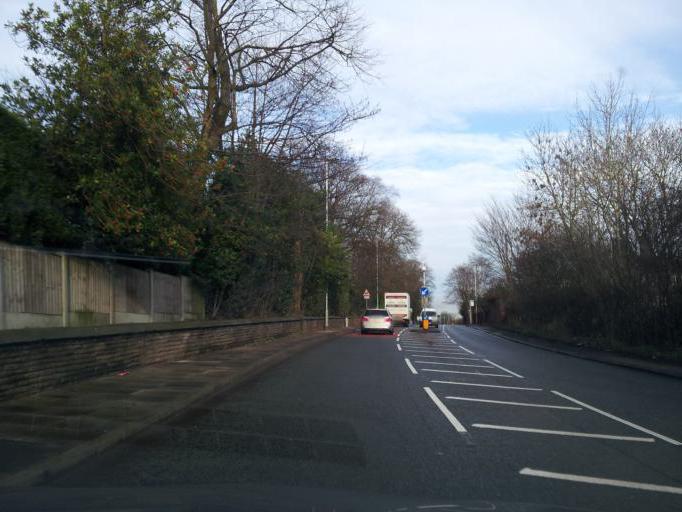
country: GB
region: England
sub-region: Manchester
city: Heywood
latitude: 53.5797
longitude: -2.2145
